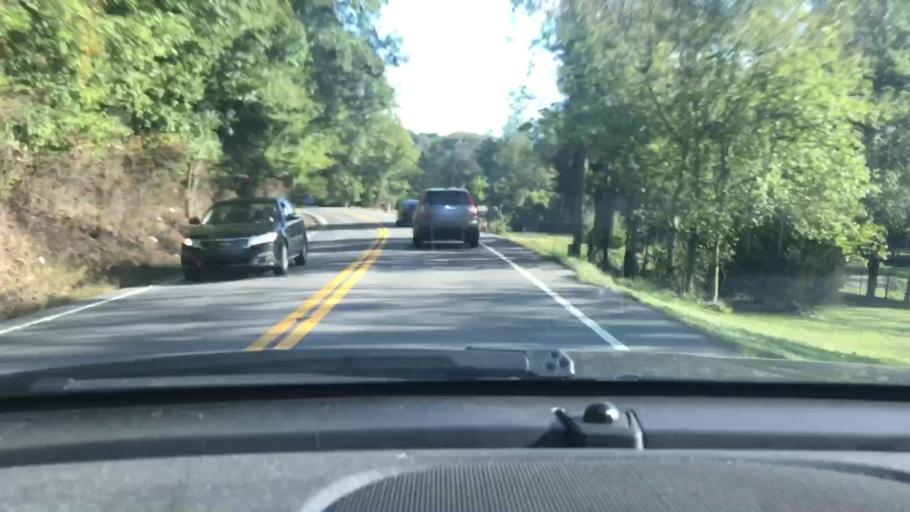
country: US
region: Tennessee
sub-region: Sumner County
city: White House
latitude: 36.4195
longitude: -86.6548
